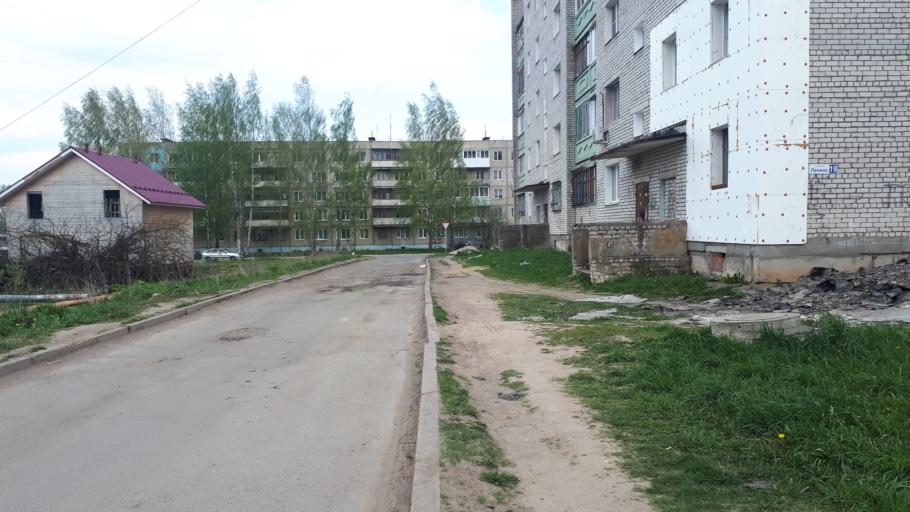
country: RU
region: Jaroslavl
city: Konstantinovskiy
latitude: 57.8313
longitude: 39.5897
